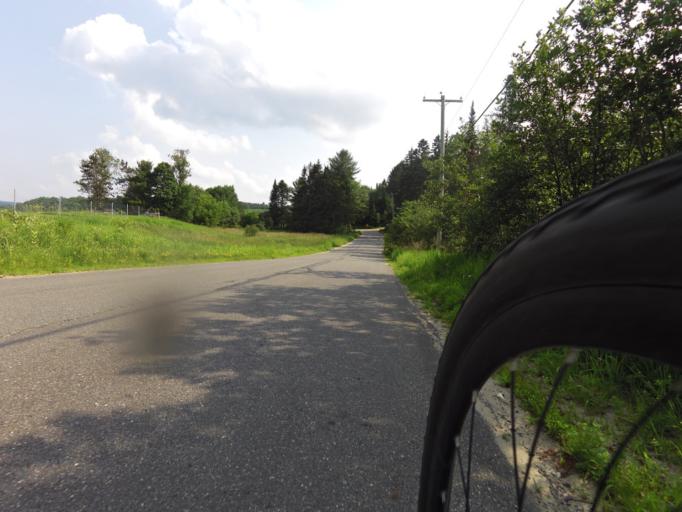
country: CA
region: Quebec
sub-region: Laurentides
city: Mont-Tremblant
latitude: 45.9591
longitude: -74.6020
